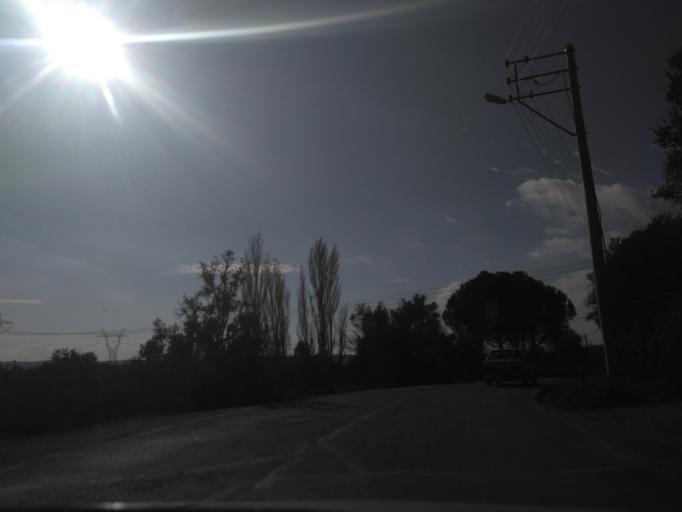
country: TR
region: Izmir
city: Buca
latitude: 38.3564
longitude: 27.2614
